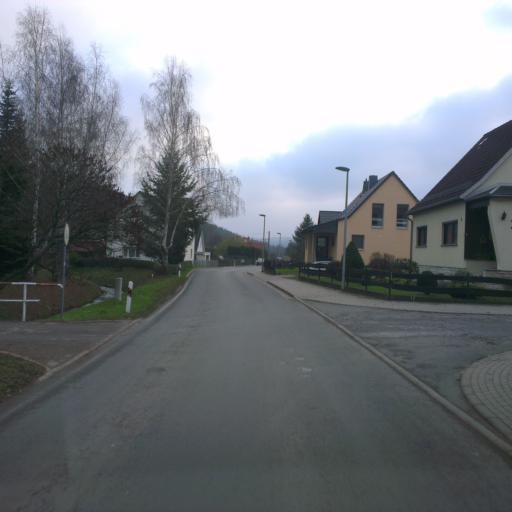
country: DE
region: Thuringia
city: Schops
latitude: 50.8373
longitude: 11.5790
